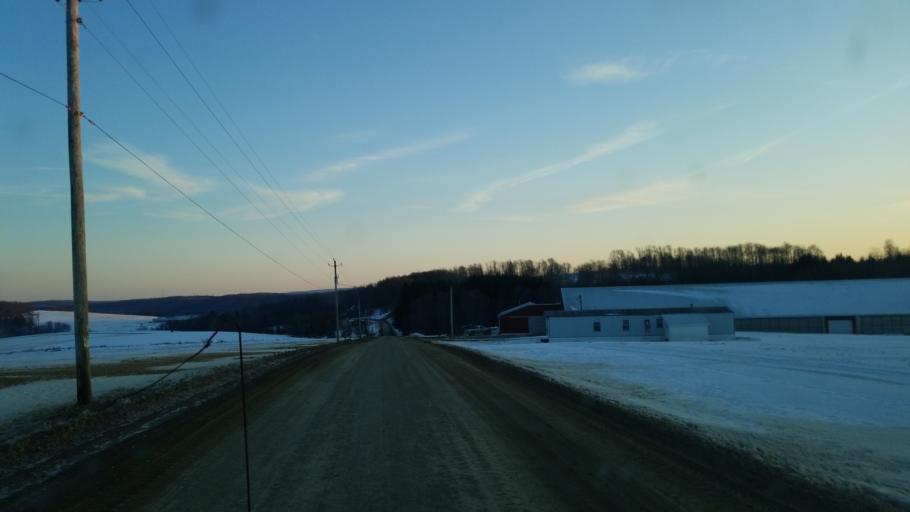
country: US
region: Pennsylvania
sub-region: Tioga County
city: Westfield
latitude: 42.0202
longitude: -77.6567
